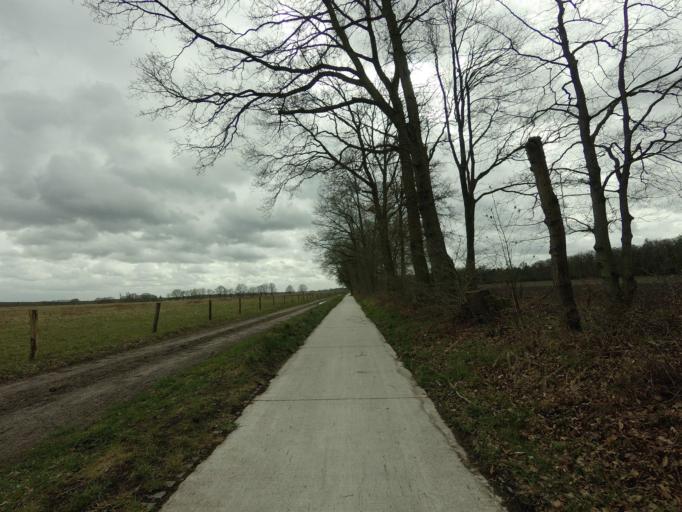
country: NL
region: Gelderland
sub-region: Gemeente Renkum
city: Heelsum
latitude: 52.0067
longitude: 5.7492
